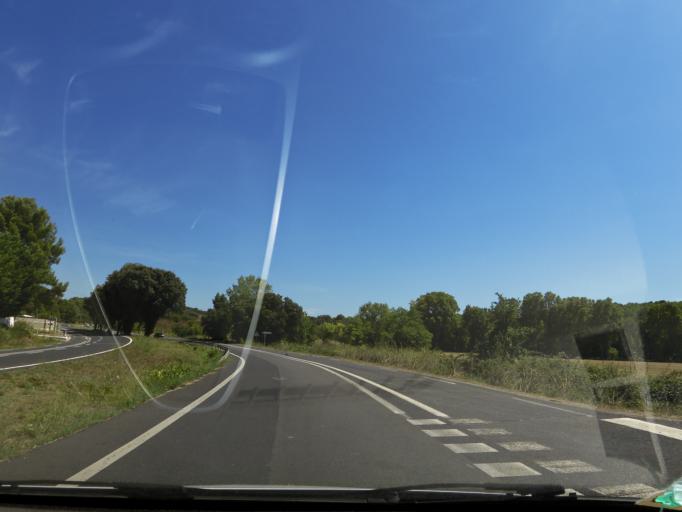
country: FR
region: Languedoc-Roussillon
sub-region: Departement de l'Herault
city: Clapiers
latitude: 43.6484
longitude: 3.8845
